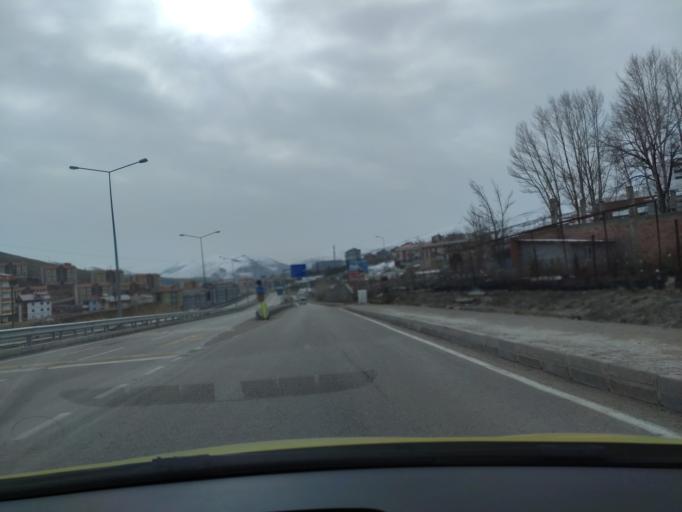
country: TR
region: Bayburt
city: Bayburt
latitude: 40.2614
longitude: 40.2094
